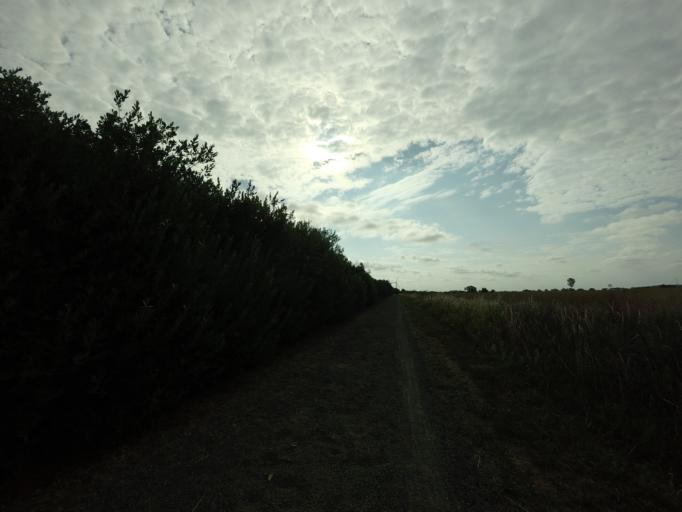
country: SE
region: Skane
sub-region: Helsingborg
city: Odakra
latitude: 56.1683
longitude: 12.7215
